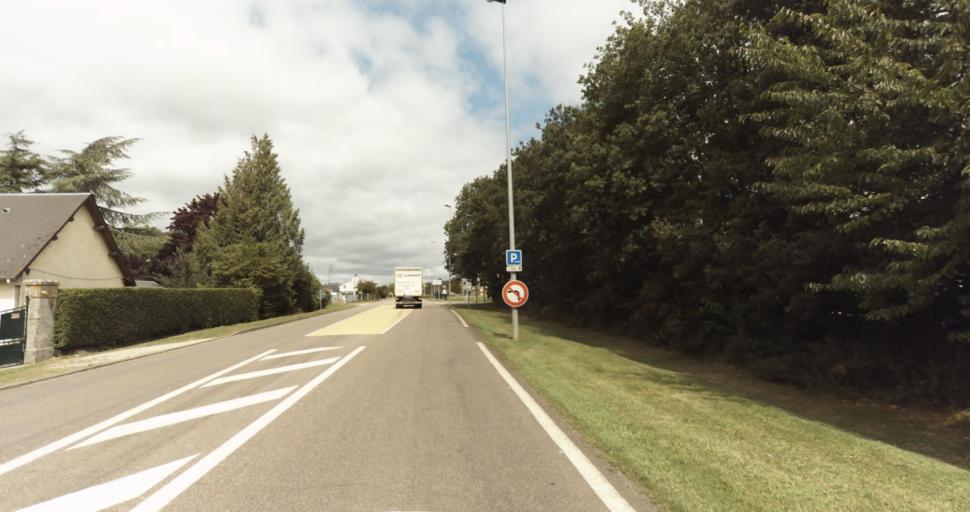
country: FR
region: Haute-Normandie
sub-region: Departement de l'Eure
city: Evreux
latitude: 48.9706
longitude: 1.1596
